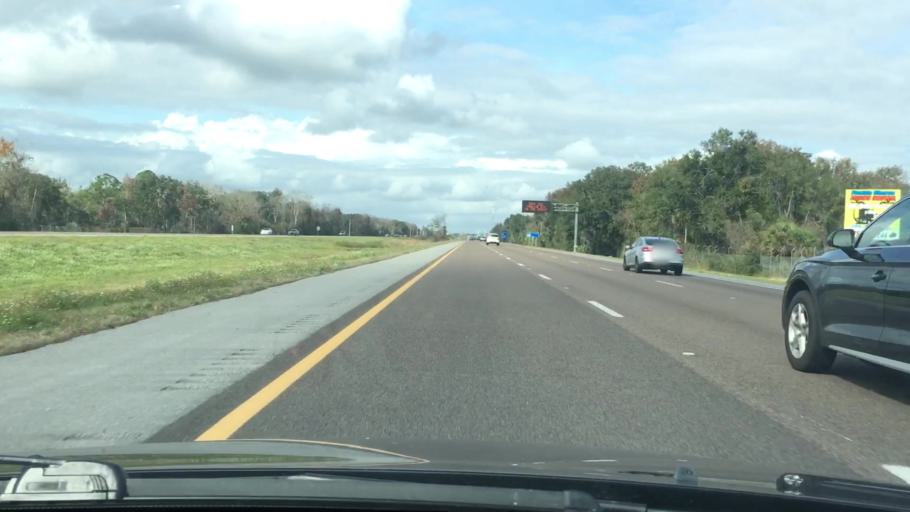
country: US
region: Florida
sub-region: Volusia County
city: Edgewater
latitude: 28.9366
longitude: -80.9439
